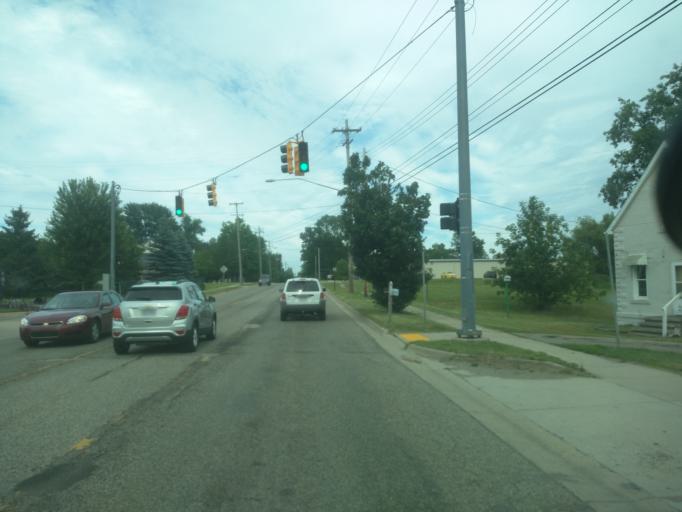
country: US
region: Michigan
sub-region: Ingham County
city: Lansing
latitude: 42.6901
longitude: -84.5293
